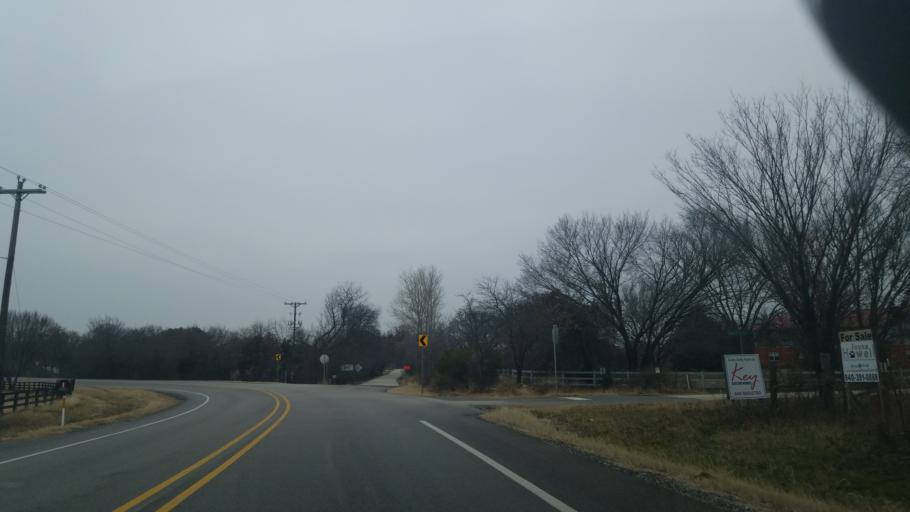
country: US
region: Texas
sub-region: Denton County
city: Argyle
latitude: 33.1343
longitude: -97.1487
